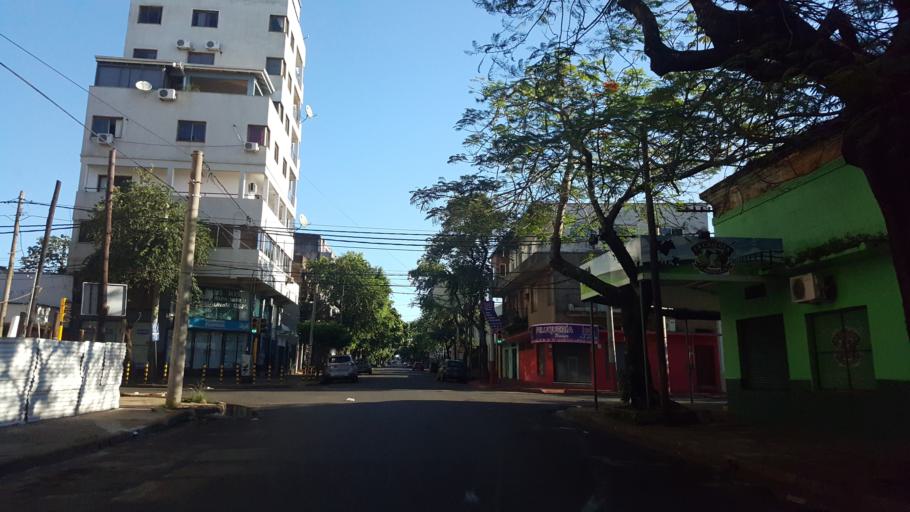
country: AR
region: Misiones
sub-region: Departamento de Capital
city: Posadas
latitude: -27.3669
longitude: -55.9000
